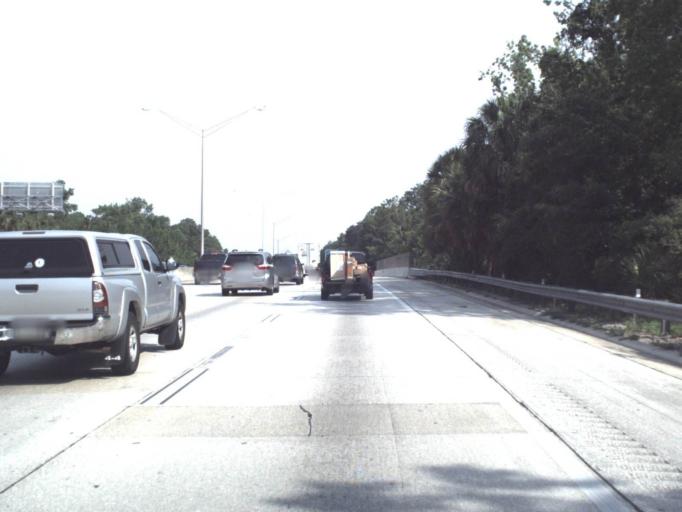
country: US
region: Florida
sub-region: Duval County
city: Jacksonville
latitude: 30.2815
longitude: -81.6206
